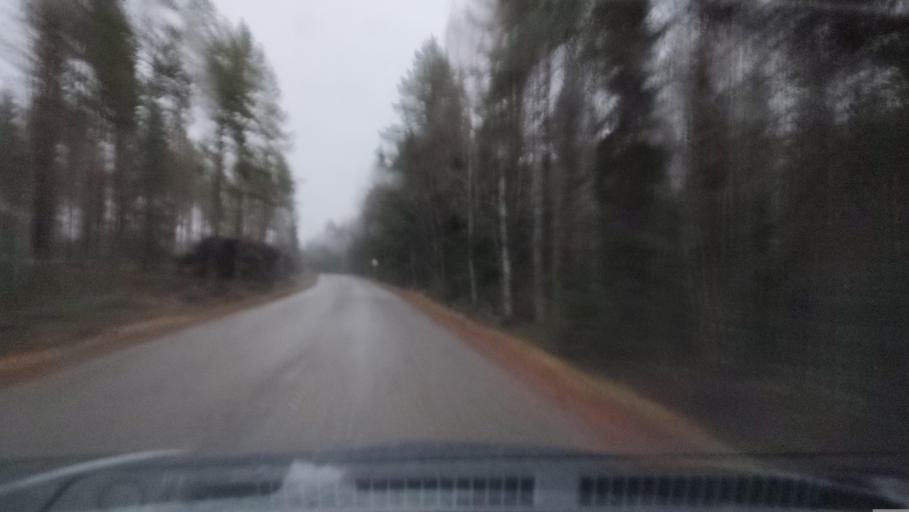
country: FI
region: Ostrobothnia
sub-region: Sydosterbotten
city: Kristinestad
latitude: 62.1477
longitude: 21.5564
